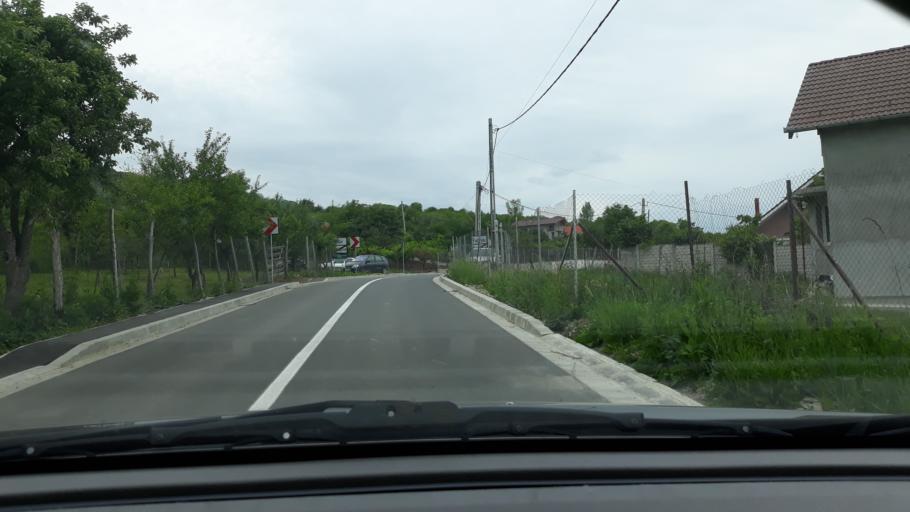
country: RO
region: Bihor
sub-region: Comuna Osorheiu
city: Osorheiu
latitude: 47.0659
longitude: 22.0311
